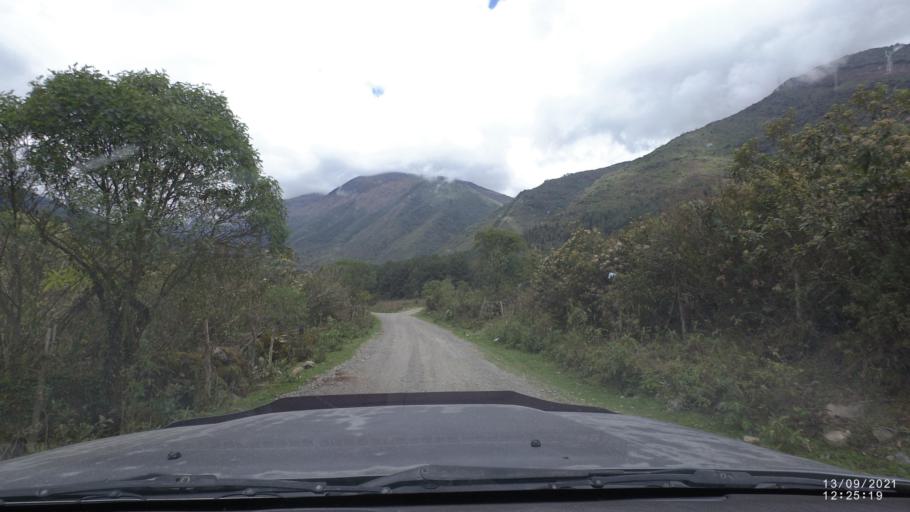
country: BO
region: Cochabamba
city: Colomi
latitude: -17.2506
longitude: -65.8168
